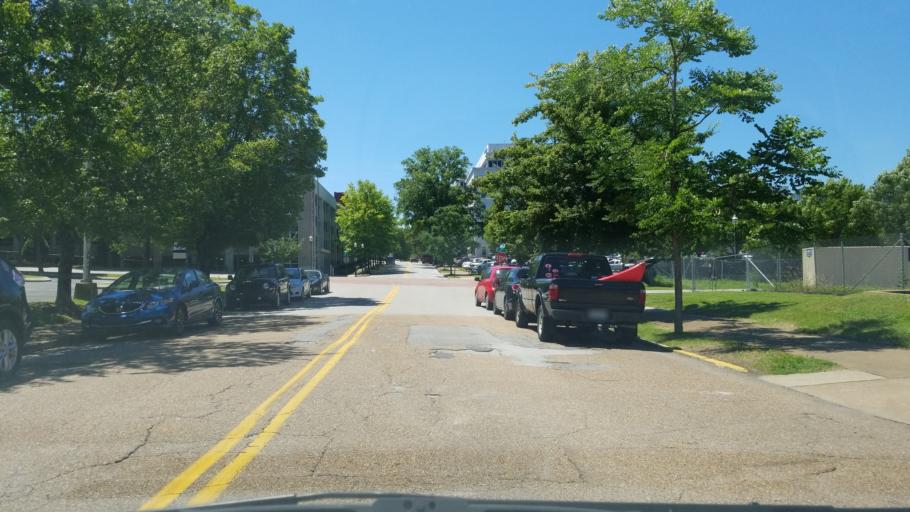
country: US
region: Tennessee
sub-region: Hamilton County
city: Chattanooga
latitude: 35.0528
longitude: -85.3065
